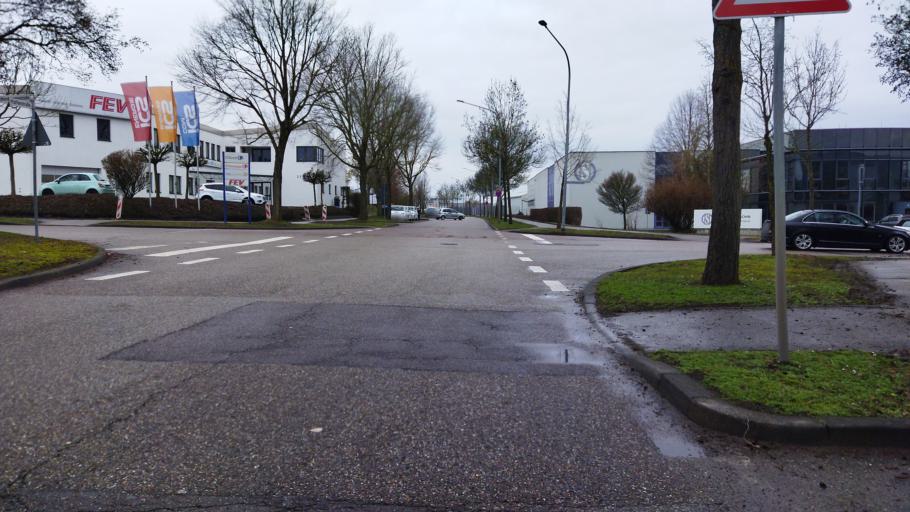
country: DE
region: Baden-Wuerttemberg
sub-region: Regierungsbezirk Stuttgart
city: Untereisesheim
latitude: 49.1833
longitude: 9.1773
